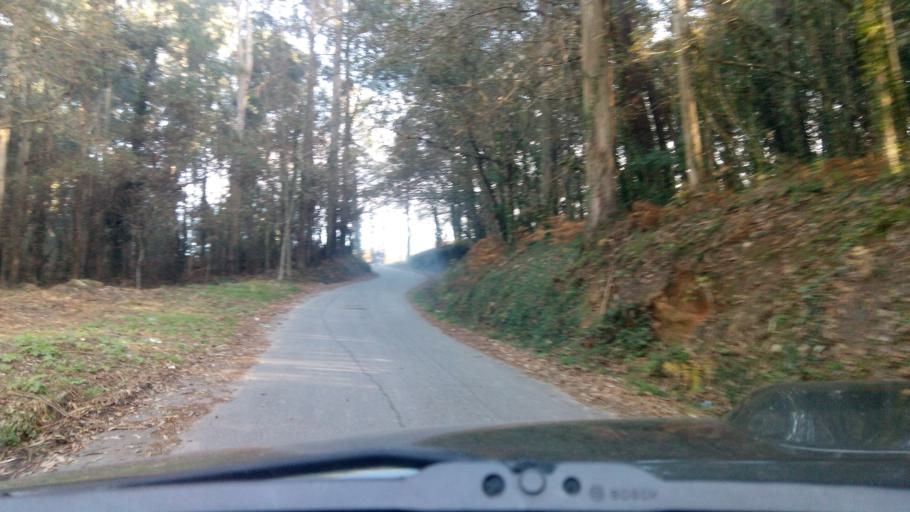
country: ES
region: Galicia
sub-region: Provincia de Pontevedra
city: Marin
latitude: 42.3560
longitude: -8.7271
